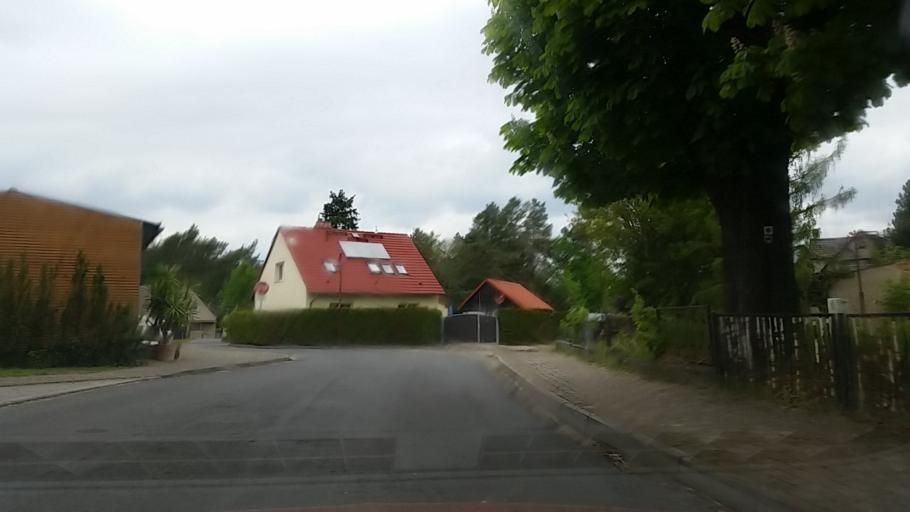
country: DE
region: Brandenburg
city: Reichenwalde
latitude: 52.2908
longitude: 13.9863
